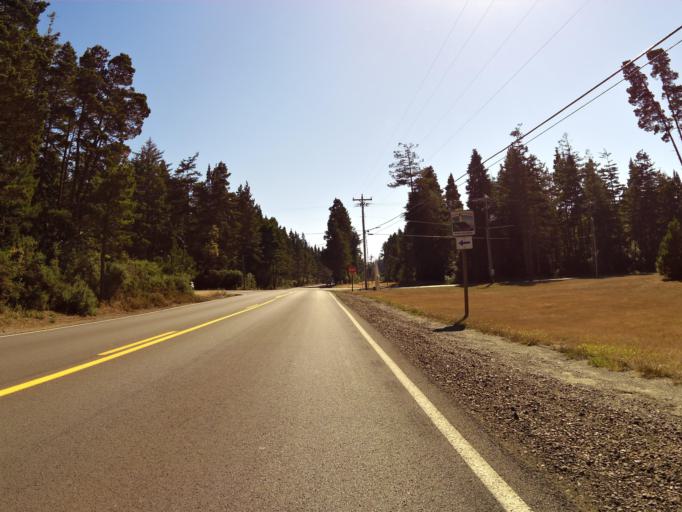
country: US
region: Oregon
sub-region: Coos County
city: Bandon
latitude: 43.1876
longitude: -124.3678
